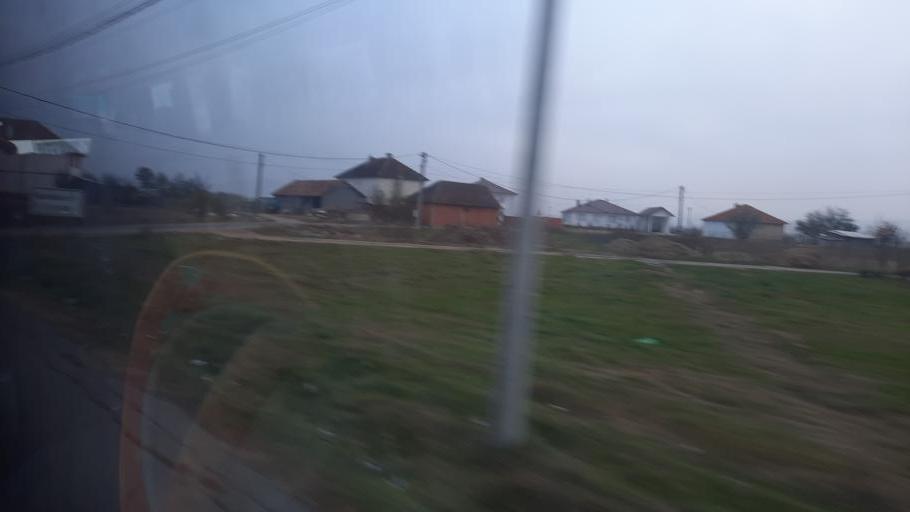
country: XK
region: Pristina
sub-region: Komuna e Drenasit
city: Glogovac
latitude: 42.6001
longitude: 20.8963
